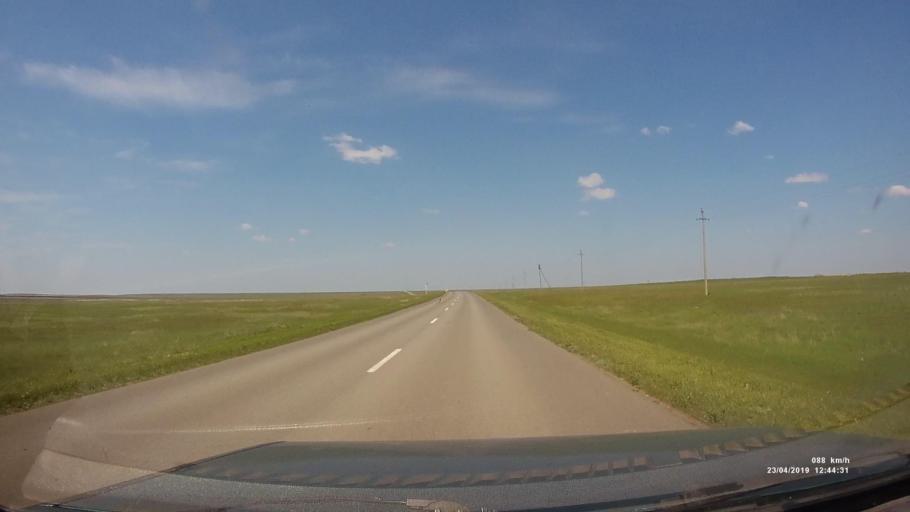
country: RU
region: Kalmykiya
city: Yashalta
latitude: 46.4778
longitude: 42.6471
